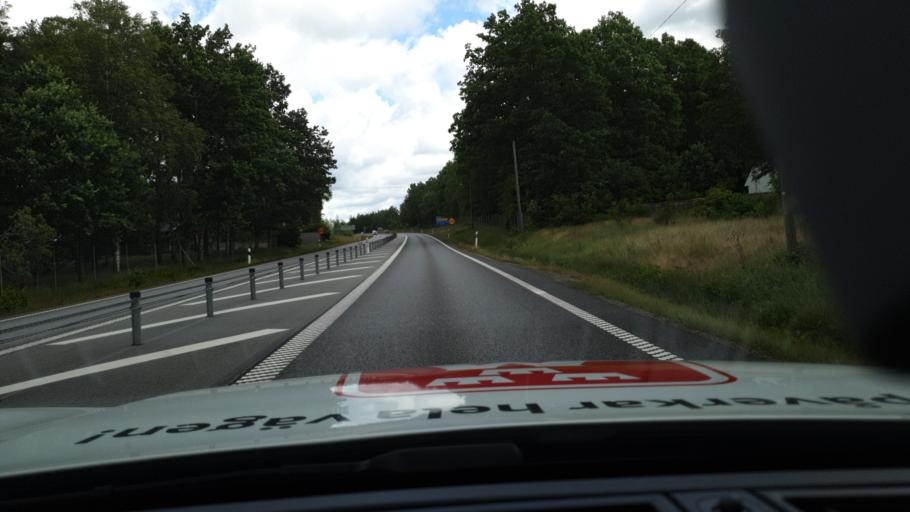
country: SE
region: Kronoberg
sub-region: Ljungby Kommun
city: Ljungby
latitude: 56.7614
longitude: 13.7792
